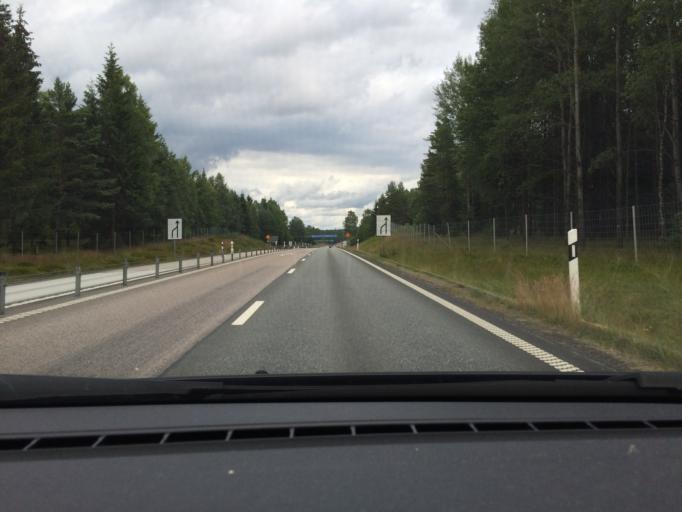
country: SE
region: Joenkoeping
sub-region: Varnamo Kommun
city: Forsheda
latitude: 57.1752
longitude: 13.9144
